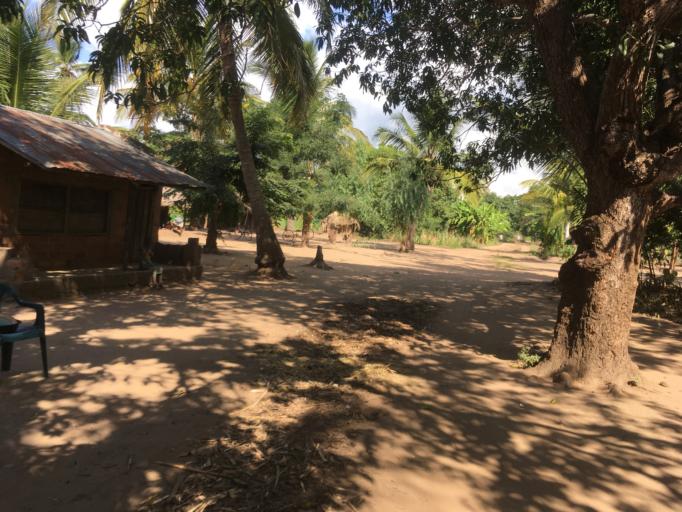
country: MZ
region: Zambezia
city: Quelimane
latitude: -17.6468
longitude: 36.6854
